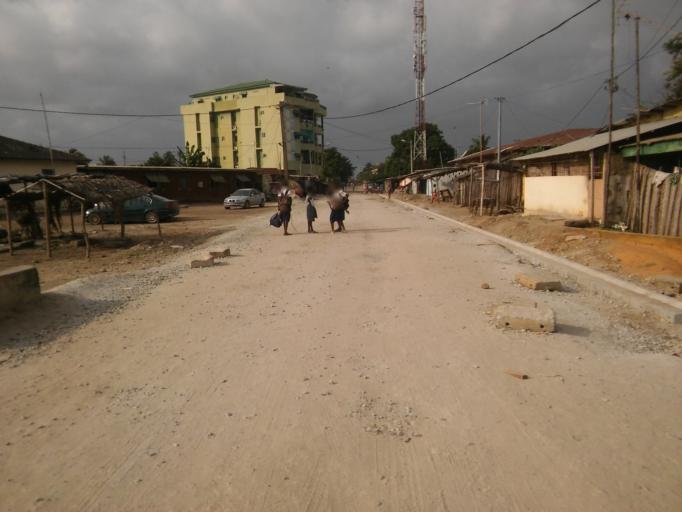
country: CI
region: Sud-Comoe
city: Grand-Bassam
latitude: 5.2087
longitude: -3.7311
